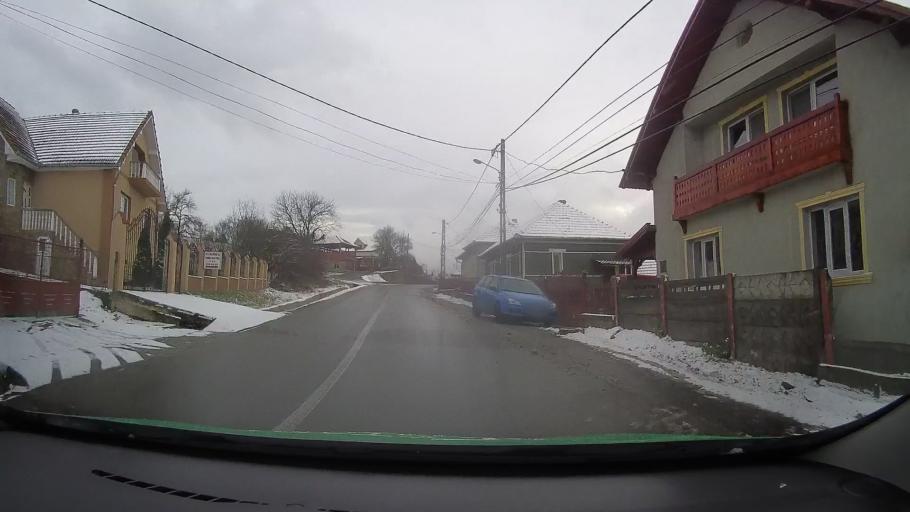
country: RO
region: Hunedoara
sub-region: Oras Hateg
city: Hateg
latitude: 45.6217
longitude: 22.9382
